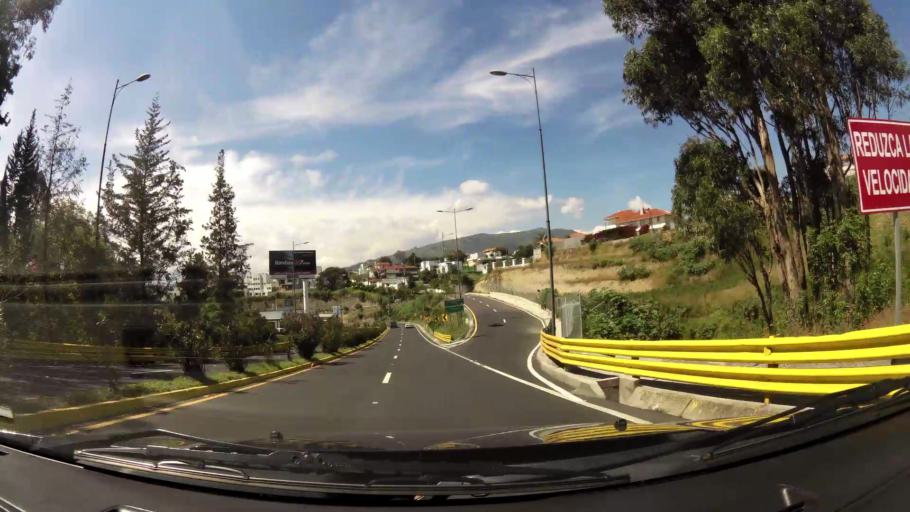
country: EC
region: Pichincha
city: Quito
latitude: -0.2056
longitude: -78.4353
